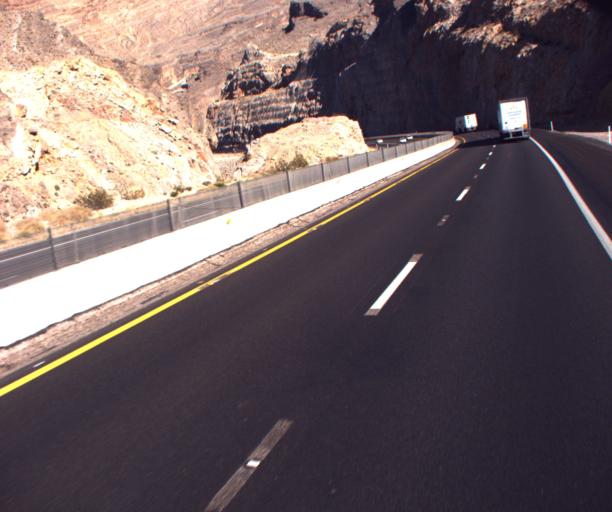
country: US
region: Arizona
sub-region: Mohave County
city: Beaver Dam
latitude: 36.9180
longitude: -113.8656
